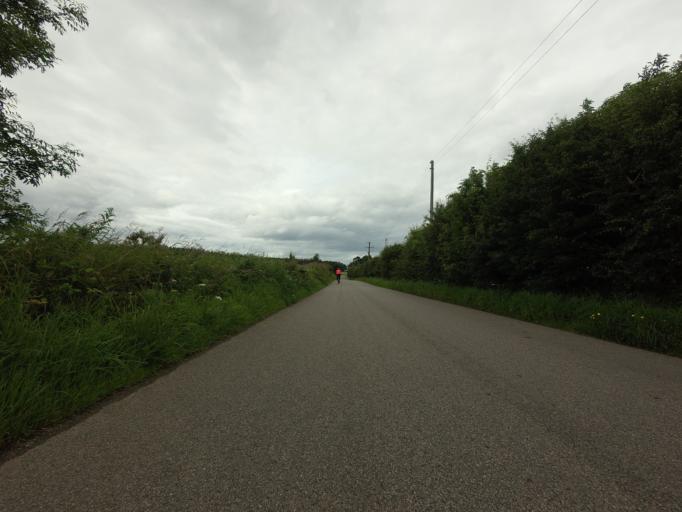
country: GB
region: Scotland
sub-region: Moray
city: Forres
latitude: 57.5979
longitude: -3.7183
